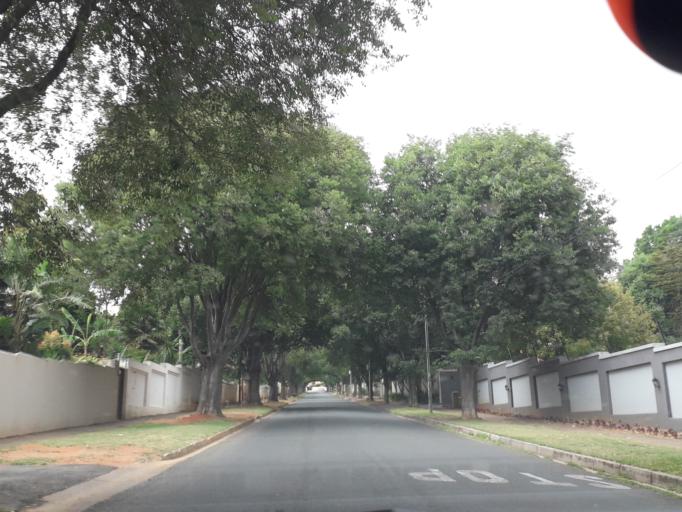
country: ZA
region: Gauteng
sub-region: City of Johannesburg Metropolitan Municipality
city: Johannesburg
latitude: -26.1363
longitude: 28.0851
